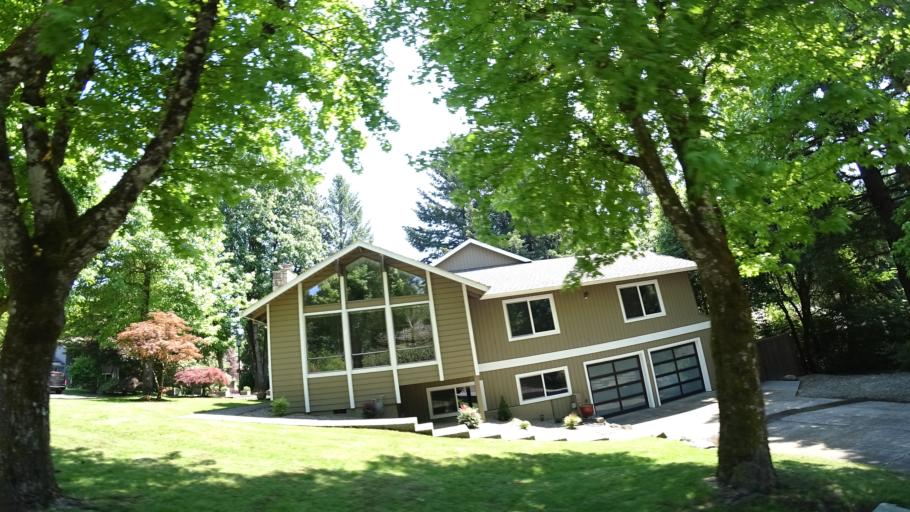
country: US
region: Oregon
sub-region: Washington County
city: Metzger
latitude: 45.4298
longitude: -122.7210
